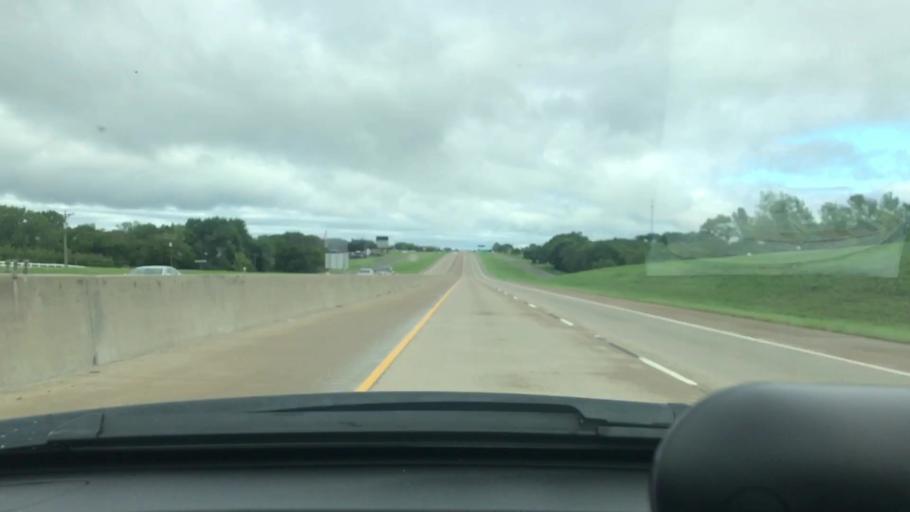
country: US
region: Texas
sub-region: Grayson County
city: Van Alstyne
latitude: 33.4418
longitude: -96.5998
